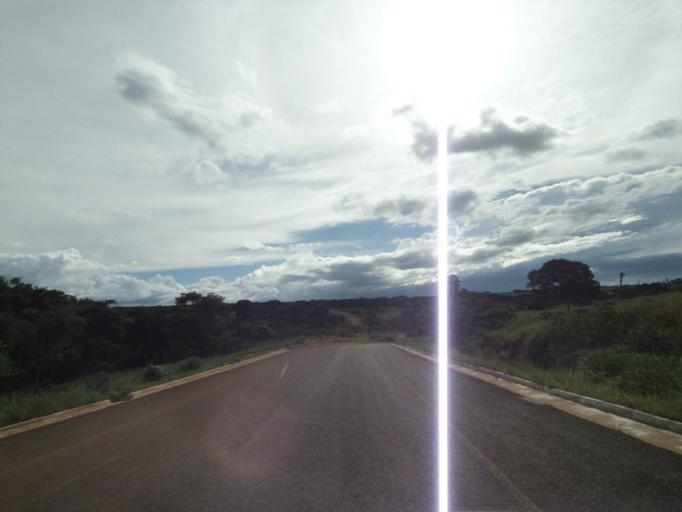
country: BR
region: Goias
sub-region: Jaragua
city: Jaragua
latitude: -15.8704
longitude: -49.4131
